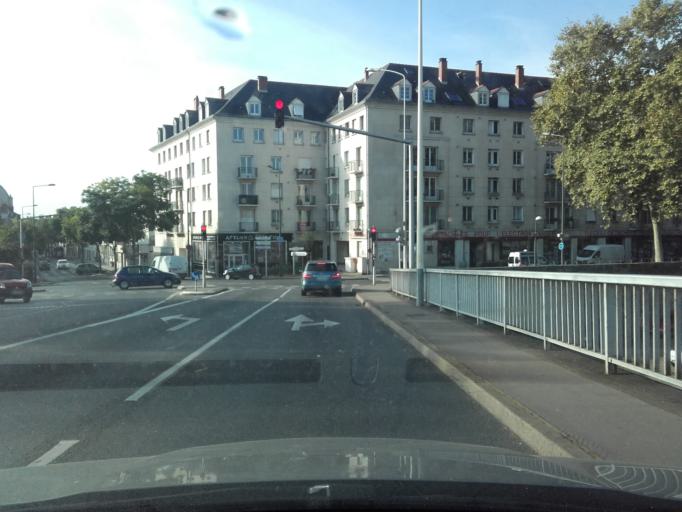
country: FR
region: Centre
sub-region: Departement d'Indre-et-Loire
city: Tours
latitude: 47.3980
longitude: 0.6995
